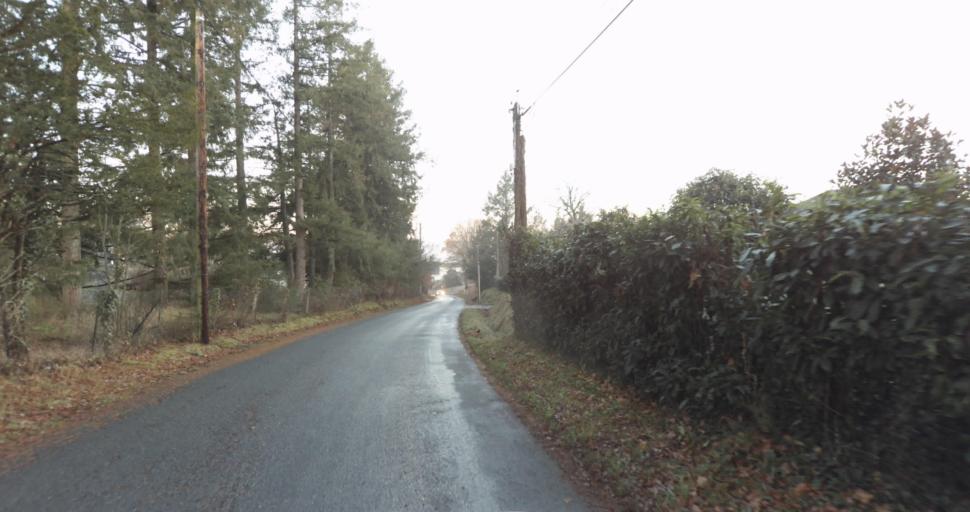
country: FR
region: Limousin
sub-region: Departement de la Haute-Vienne
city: Aixe-sur-Vienne
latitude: 45.8160
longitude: 1.1490
